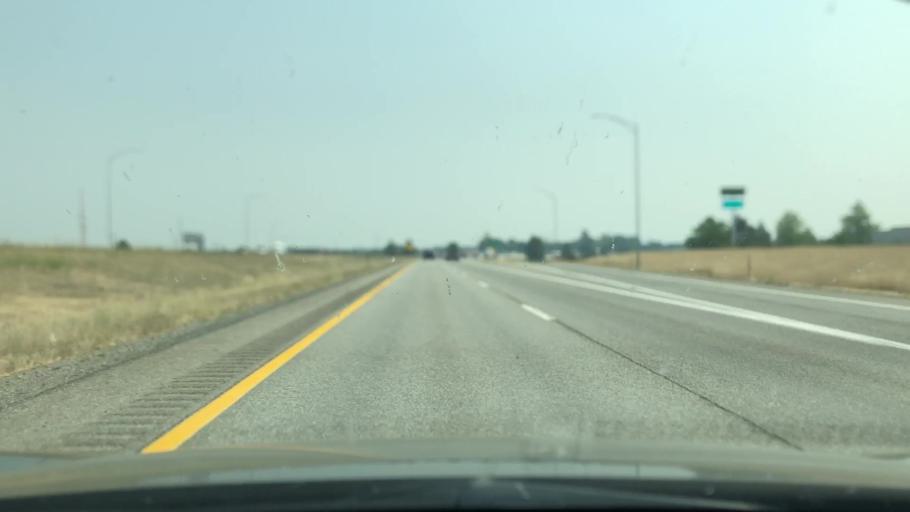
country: US
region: Idaho
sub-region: Kootenai County
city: Post Falls
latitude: 47.7071
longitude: -117.0071
